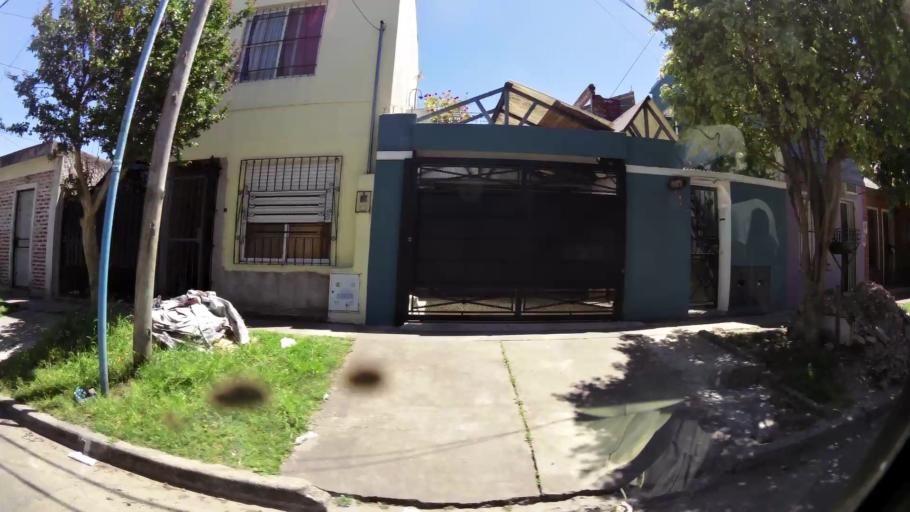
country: AR
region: Buenos Aires
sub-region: Partido de Quilmes
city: Quilmes
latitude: -34.7169
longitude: -58.3112
